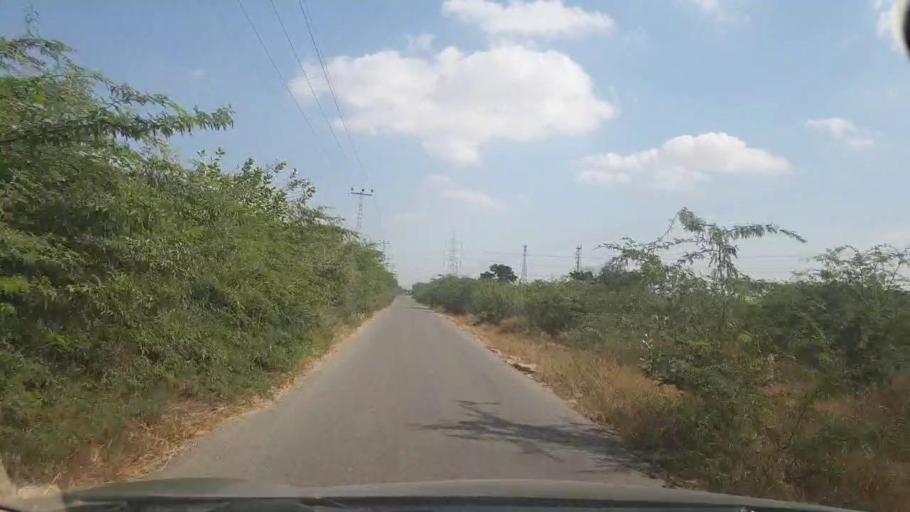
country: PK
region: Sindh
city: Malir Cantonment
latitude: 25.0188
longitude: 67.3619
